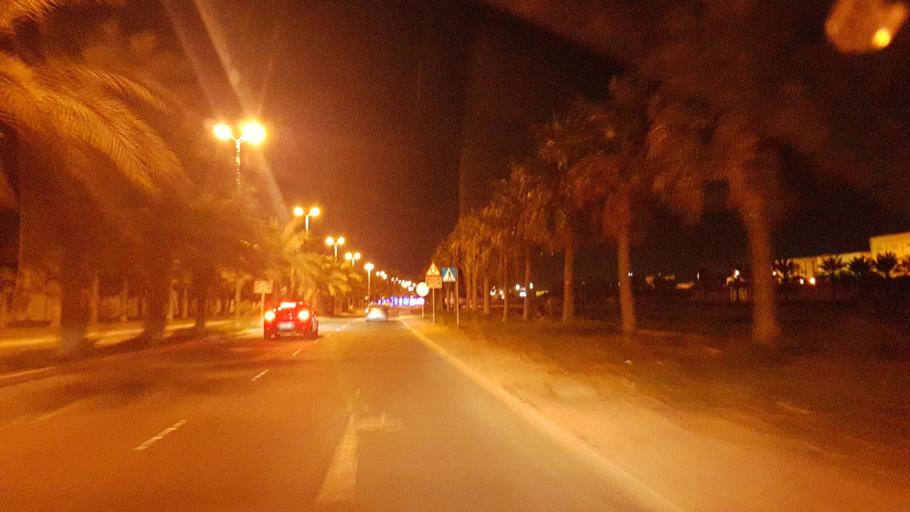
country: BH
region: Muharraq
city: Al Hadd
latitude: 26.2809
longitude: 50.6588
